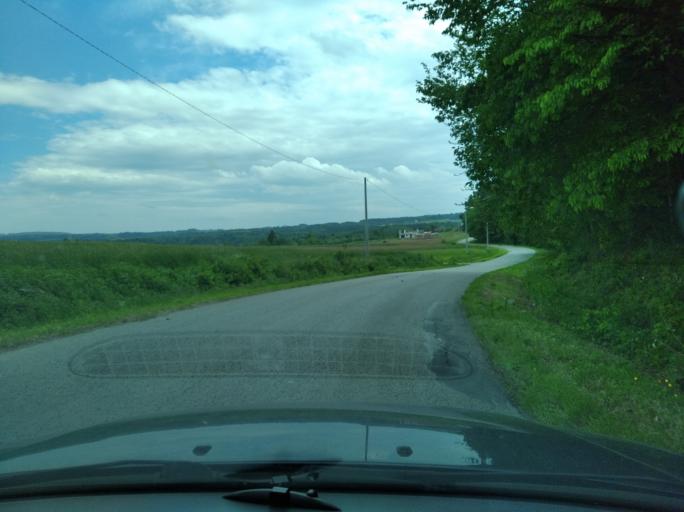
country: PL
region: Subcarpathian Voivodeship
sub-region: Powiat ropczycko-sedziszowski
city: Ropczyce
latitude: 50.0068
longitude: 21.6140
